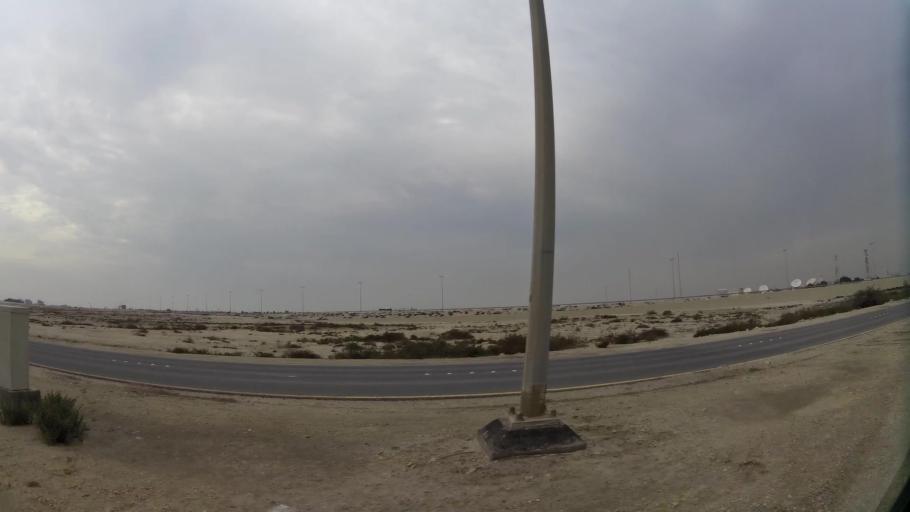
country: BH
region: Northern
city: Sitrah
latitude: 26.0683
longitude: 50.6163
